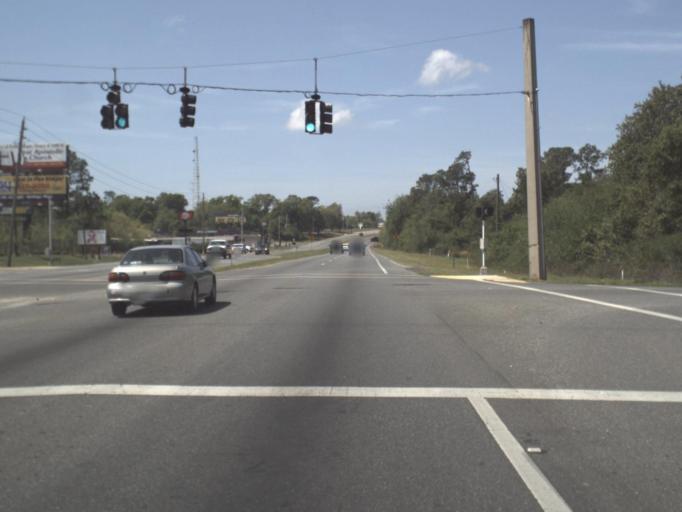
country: US
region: Florida
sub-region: Santa Rosa County
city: Bagdad
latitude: 30.6057
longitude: -87.0653
